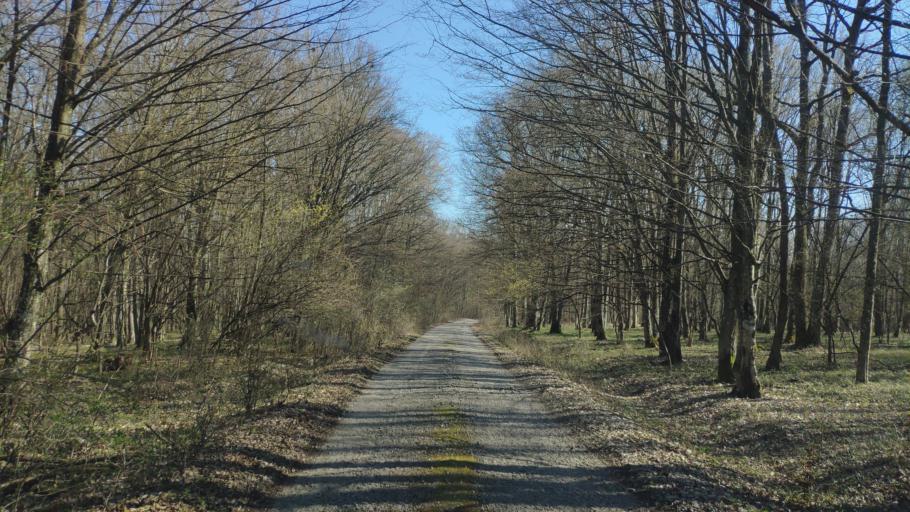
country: SK
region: Kosicky
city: Roznava
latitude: 48.5888
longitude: 20.4088
